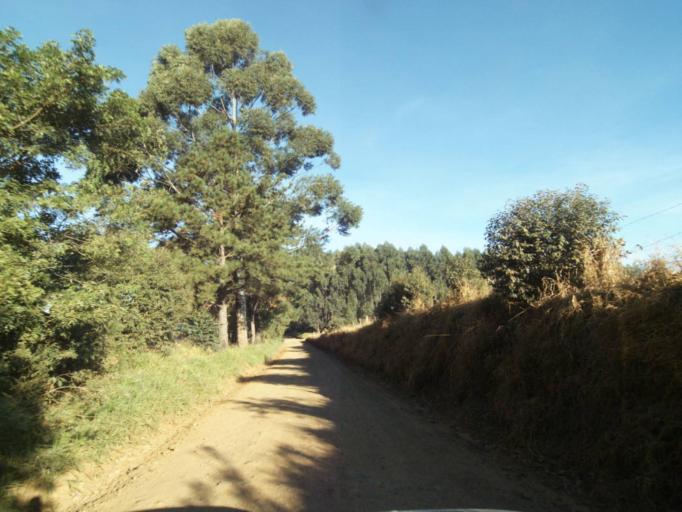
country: BR
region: Parana
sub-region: Tibagi
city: Tibagi
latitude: -24.5397
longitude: -50.6251
